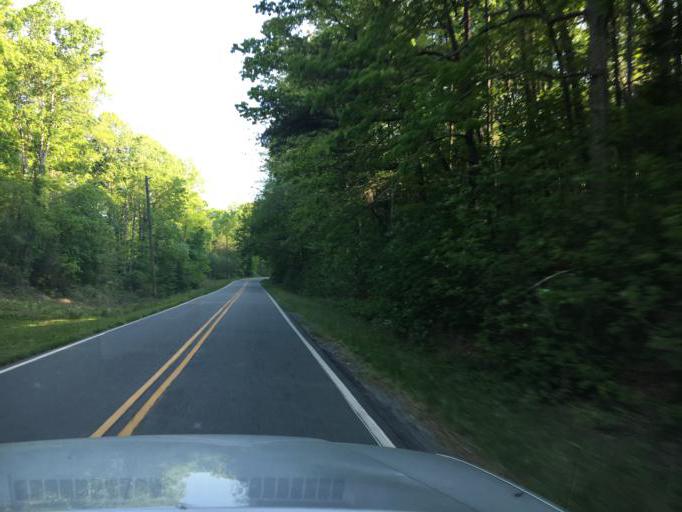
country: US
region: North Carolina
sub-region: Rutherford County
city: Rutherfordton
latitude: 35.2963
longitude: -82.0050
